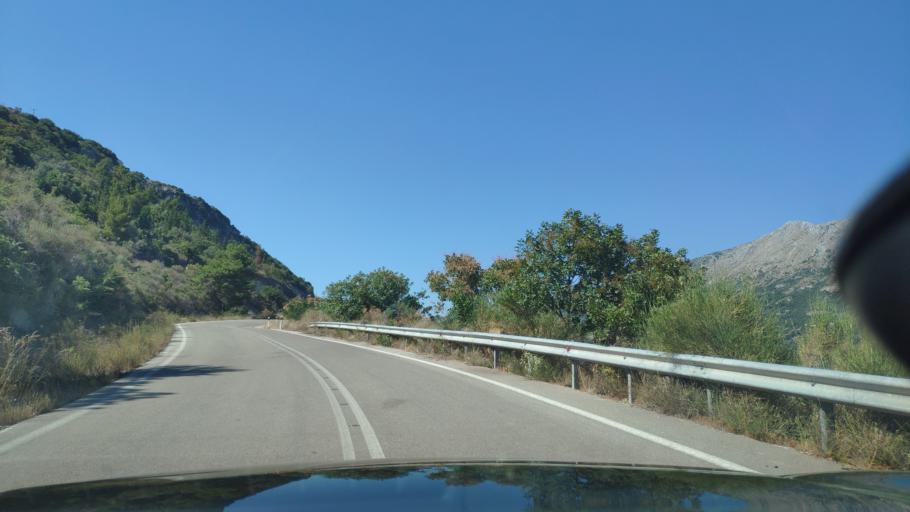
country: GR
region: Ionian Islands
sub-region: Lefkada
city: Nidri
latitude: 38.6787
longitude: 20.5970
